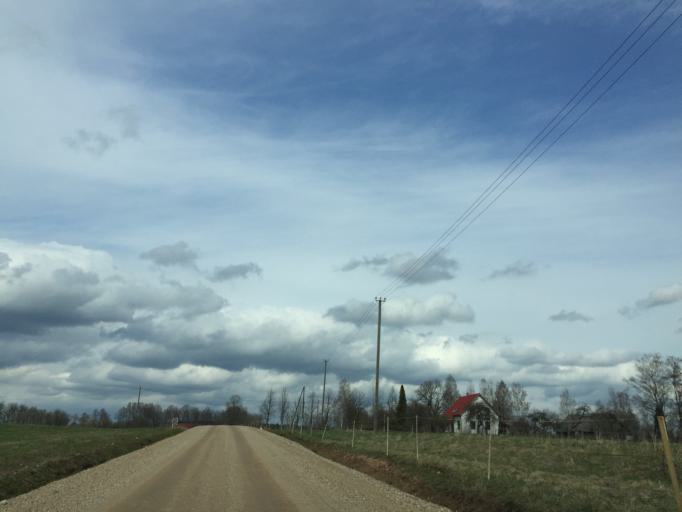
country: LV
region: Ligatne
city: Ligatne
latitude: 57.2121
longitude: 25.0671
